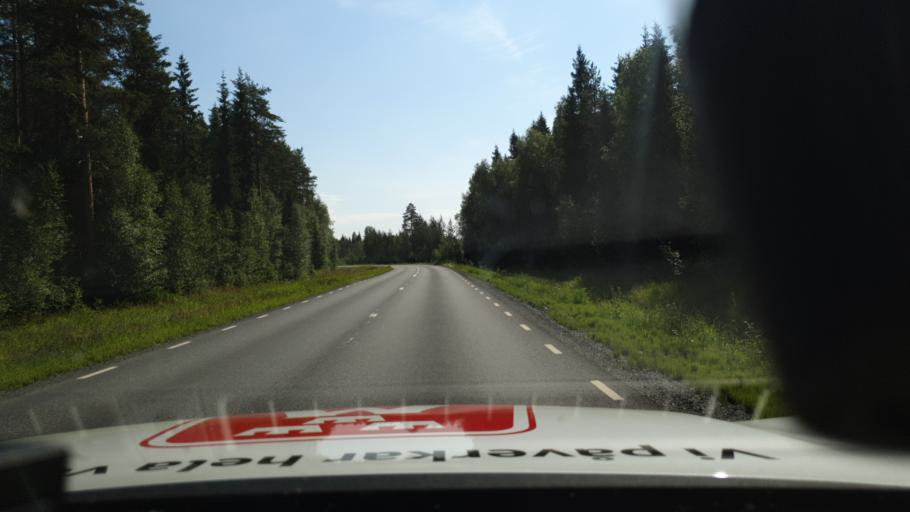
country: SE
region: Norrbotten
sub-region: Lulea Kommun
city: Gammelstad
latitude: 65.7870
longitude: 22.0997
